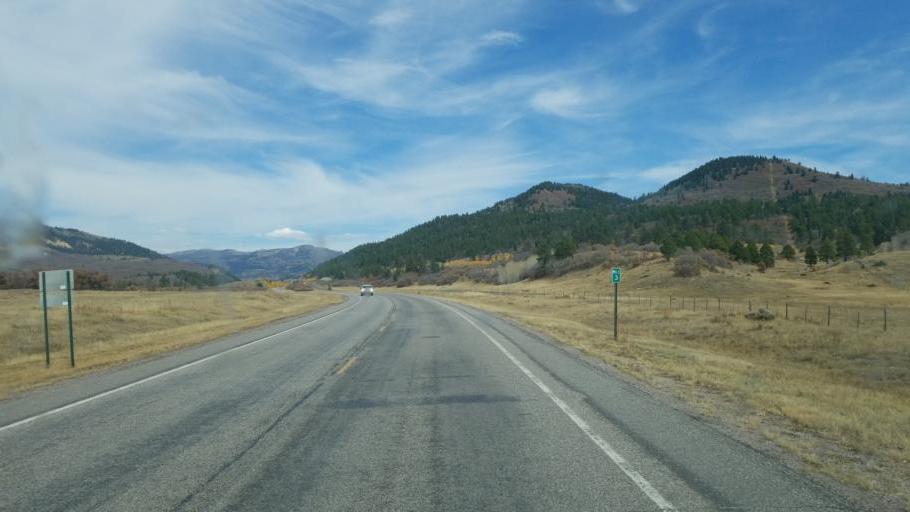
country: US
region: New Mexico
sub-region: Rio Arriba County
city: Chama
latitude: 36.9181
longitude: -106.5632
